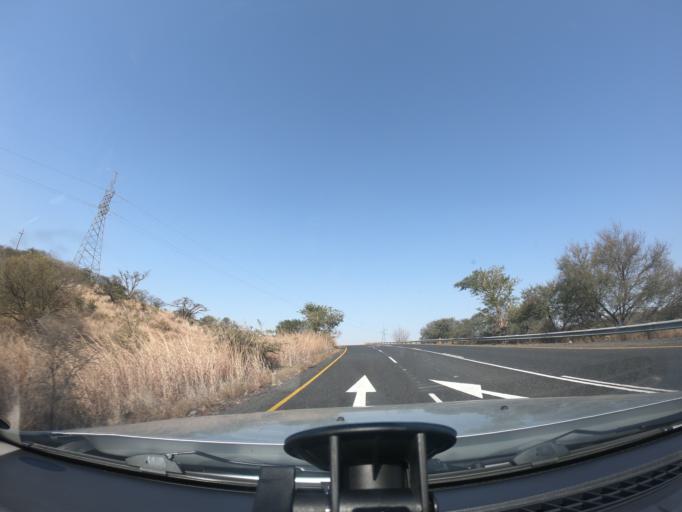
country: ZA
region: KwaZulu-Natal
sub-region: uThukela District Municipality
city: Ladysmith
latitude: -28.6884
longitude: 29.8265
